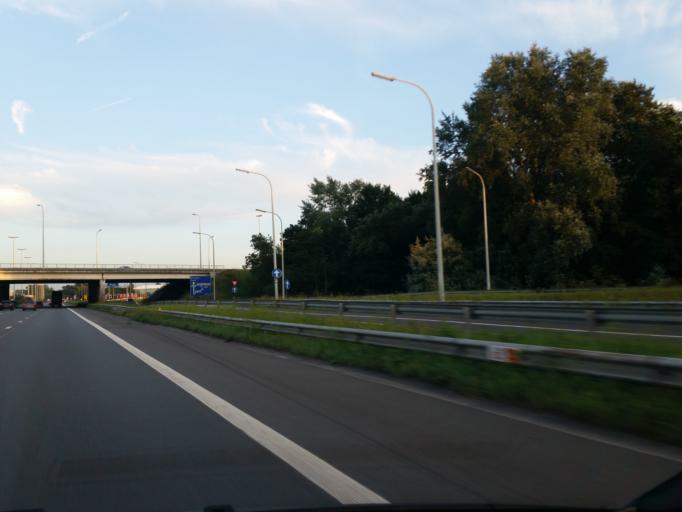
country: BE
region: Flanders
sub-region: Provincie West-Vlaanderen
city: Oostkamp
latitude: 51.1566
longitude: 3.2103
